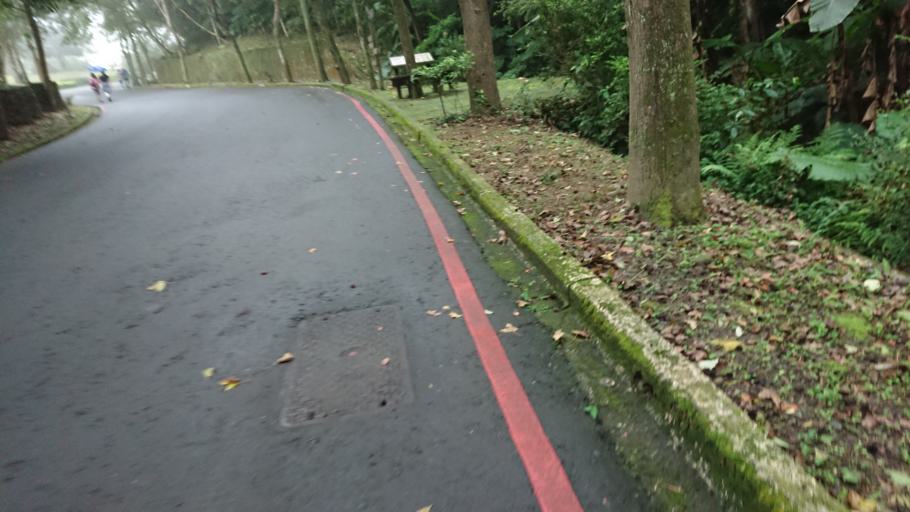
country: TW
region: Taiwan
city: Daxi
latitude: 24.8166
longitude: 121.2410
